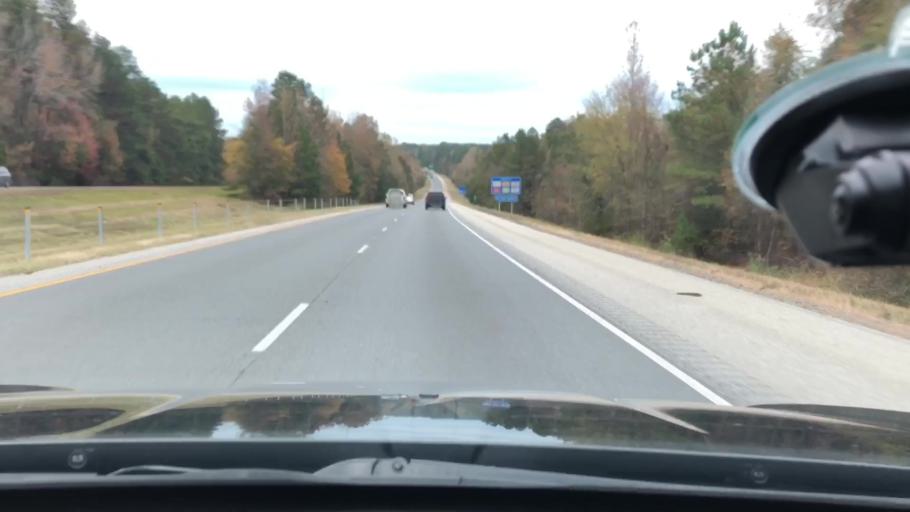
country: US
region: Arkansas
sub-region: Clark County
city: Arkadelphia
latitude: 34.0943
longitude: -93.1069
